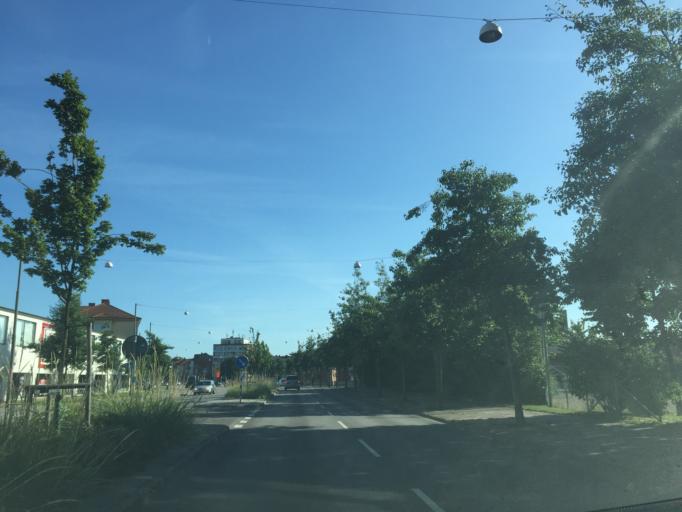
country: SE
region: Skane
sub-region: Malmo
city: Malmoe
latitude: 55.5861
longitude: 13.0190
